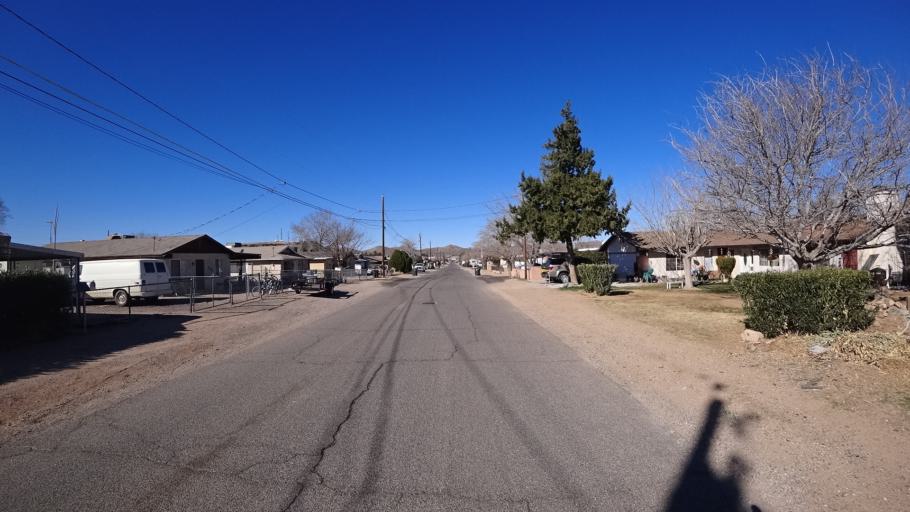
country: US
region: Arizona
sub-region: Mohave County
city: Kingman
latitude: 35.2040
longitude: -114.0255
